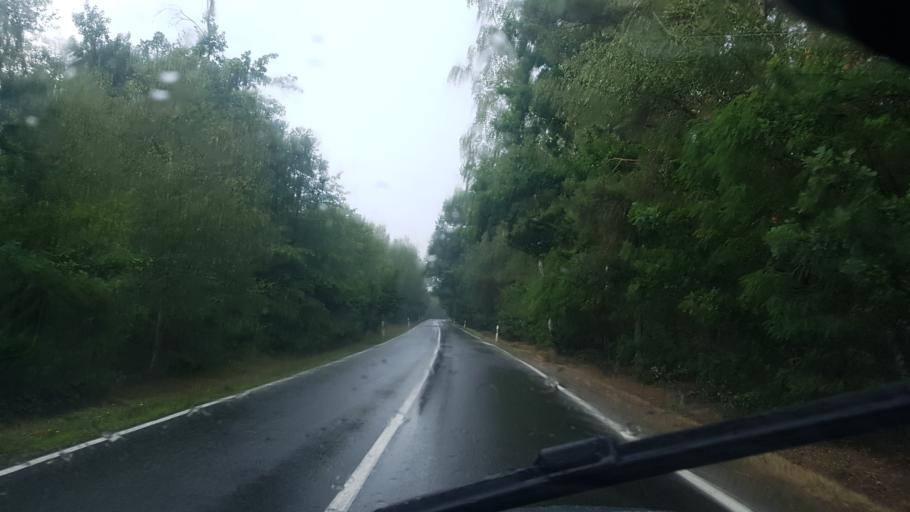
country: DE
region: Saxony
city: Bernsdorf
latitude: 51.3669
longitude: 14.1100
